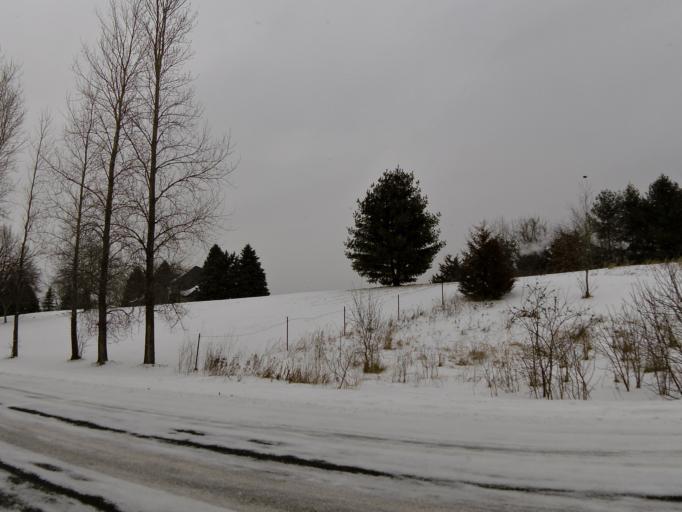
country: US
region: Minnesota
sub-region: Washington County
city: Lake Elmo
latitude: 44.9739
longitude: -92.8430
